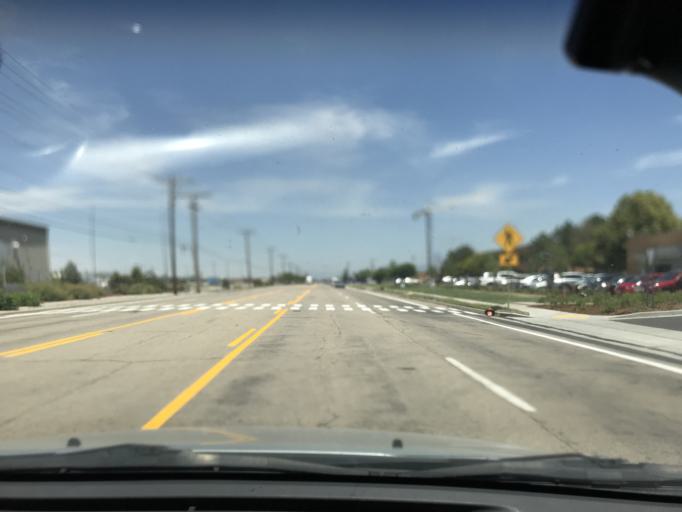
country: US
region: Utah
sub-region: Salt Lake County
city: Salt Lake City
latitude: 40.7784
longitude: -111.9535
